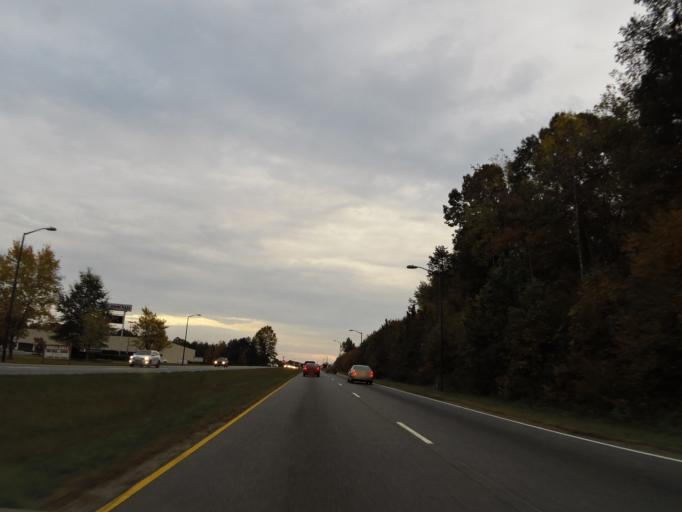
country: US
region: North Carolina
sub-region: Catawba County
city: Longview
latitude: 35.7520
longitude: -81.3711
